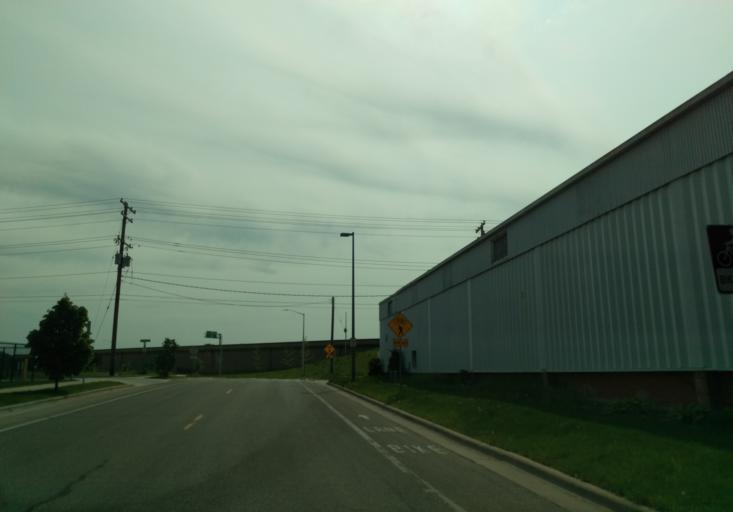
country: US
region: Wisconsin
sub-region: Dane County
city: Shorewood Hills
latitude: 43.0328
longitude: -89.4605
